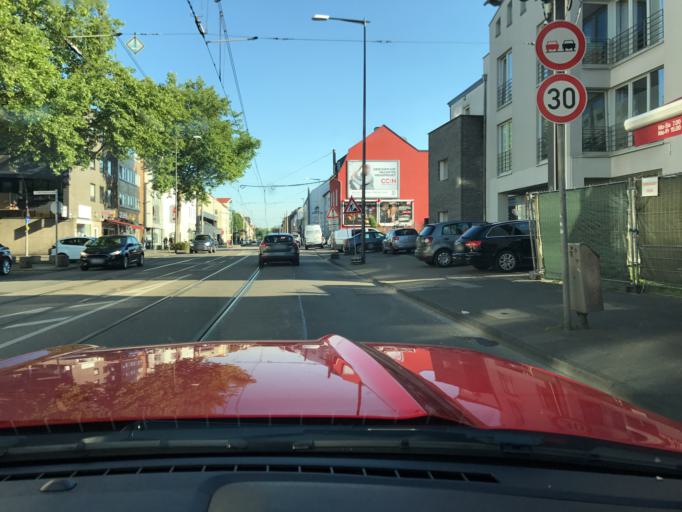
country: DE
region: North Rhine-Westphalia
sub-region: Regierungsbezirk Koln
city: Nippes
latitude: 50.9846
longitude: 6.9472
